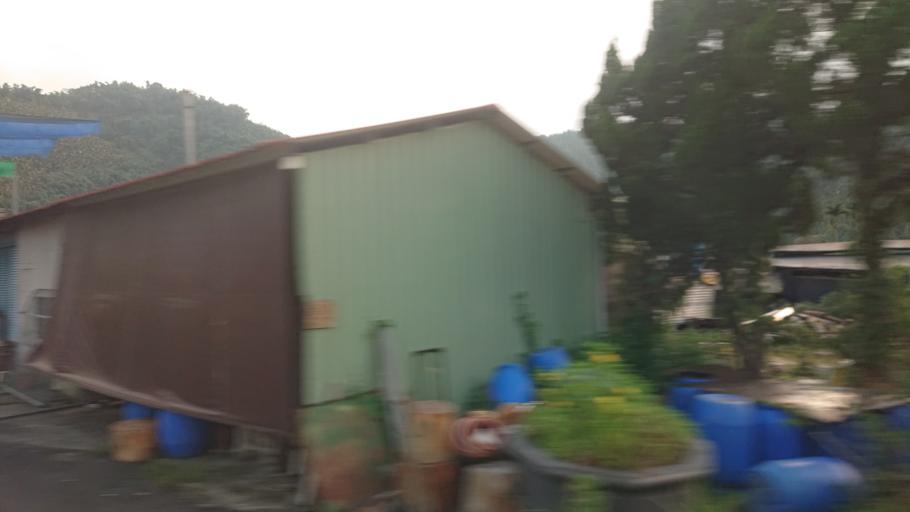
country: TW
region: Taiwan
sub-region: Nantou
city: Puli
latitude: 23.9693
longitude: 120.9976
